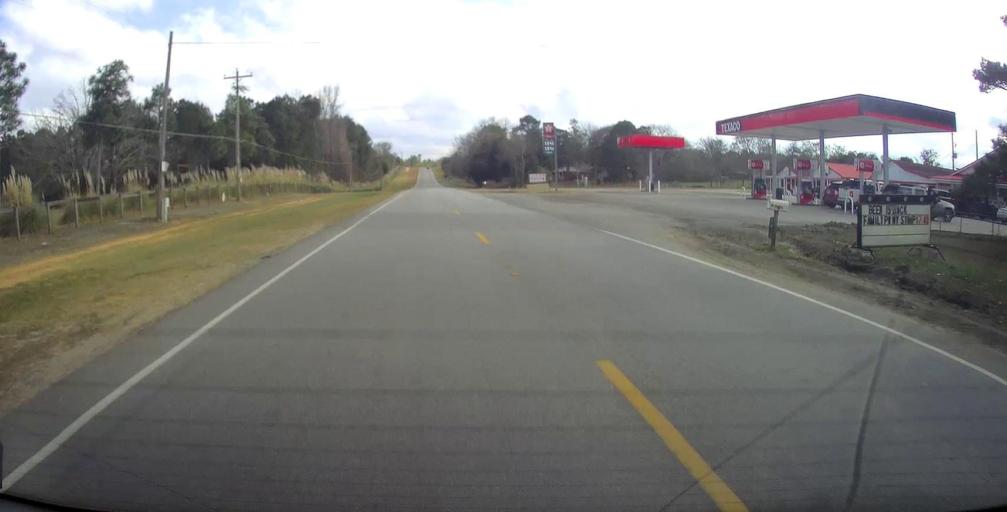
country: US
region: Georgia
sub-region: Marion County
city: Buena Vista
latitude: 32.4570
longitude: -84.5373
